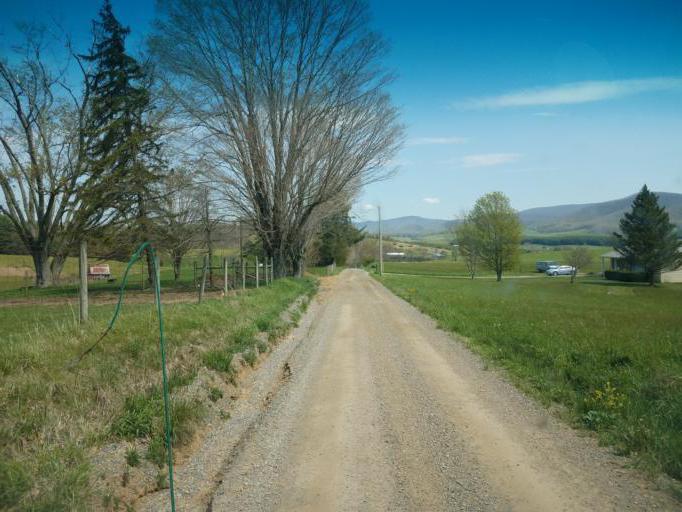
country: US
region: Virginia
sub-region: Smyth County
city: Marion
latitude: 36.7797
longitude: -81.4603
